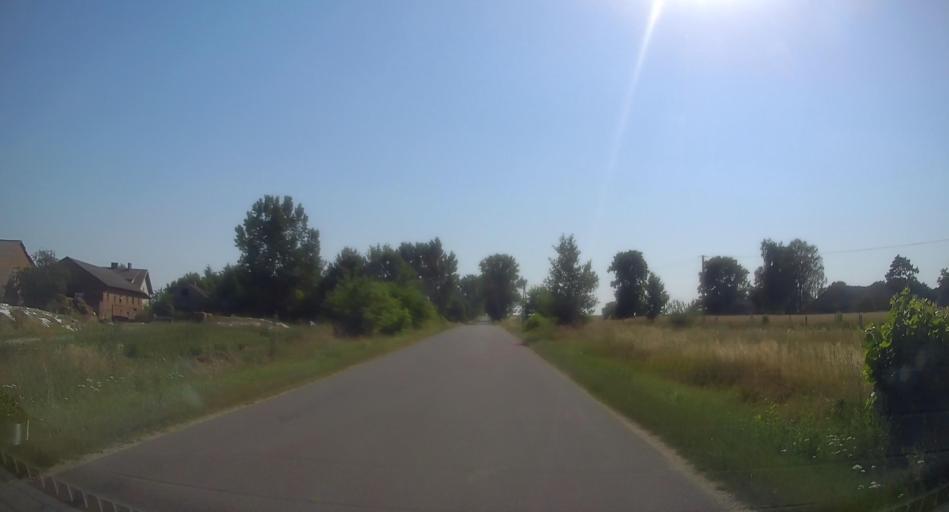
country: PL
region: Lodz Voivodeship
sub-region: Powiat skierniewicki
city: Kaweczyn Nowy
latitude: 51.8769
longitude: 20.2129
